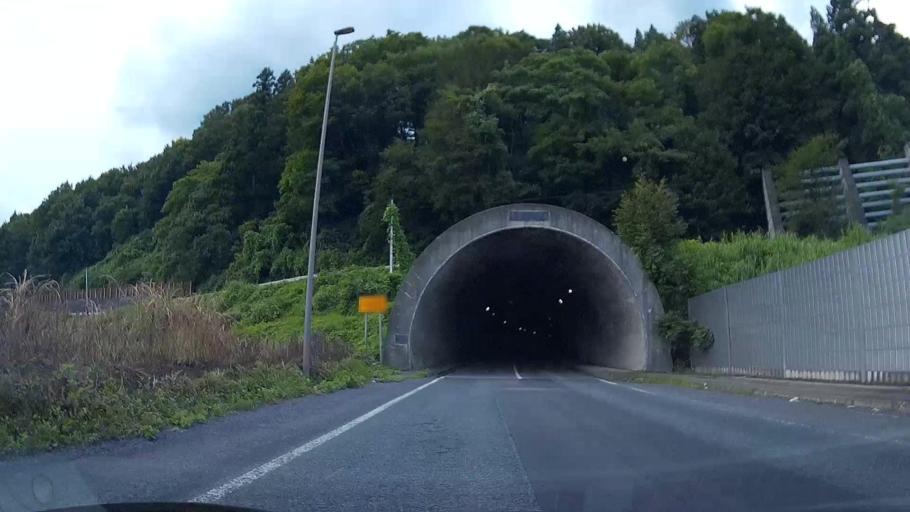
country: JP
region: Nagano
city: Iiyama
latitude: 36.9867
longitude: 138.5626
